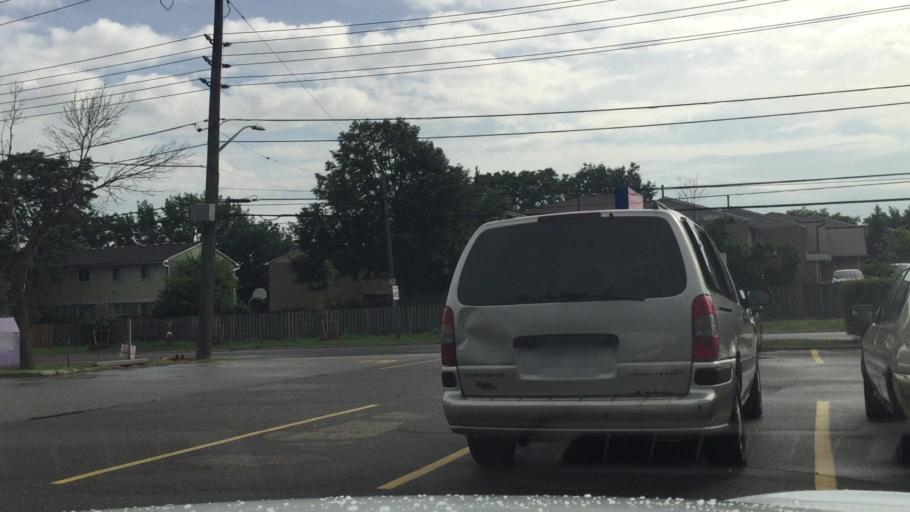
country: CA
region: Ontario
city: Mississauga
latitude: 43.5647
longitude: -79.6378
